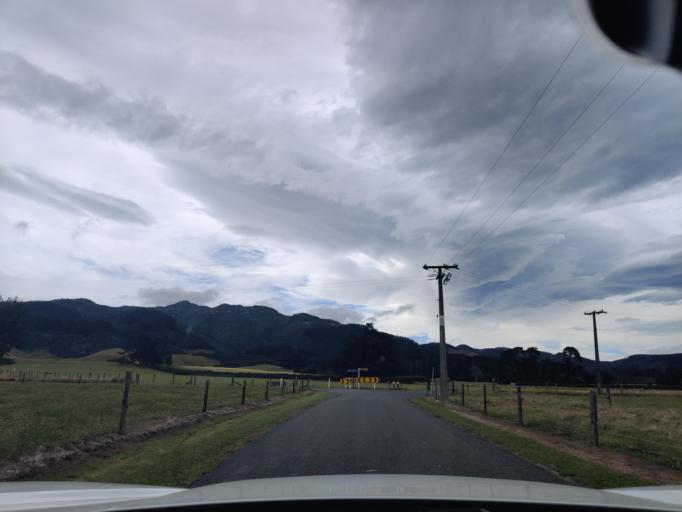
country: NZ
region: Wellington
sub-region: Masterton District
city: Masterton
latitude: -41.0301
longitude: 175.4462
